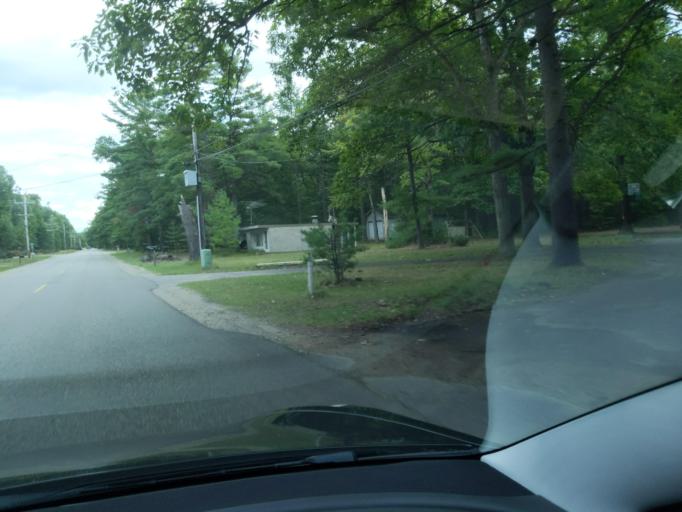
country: US
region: Michigan
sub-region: Kalkaska County
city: Rapid City
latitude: 44.8500
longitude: -85.3131
